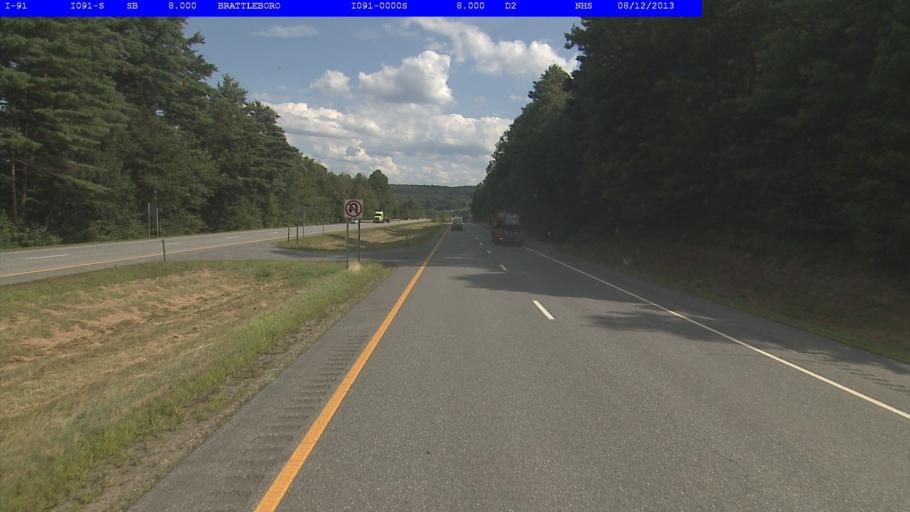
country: US
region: Vermont
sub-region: Windham County
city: Brattleboro
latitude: 42.8420
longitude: -72.5715
